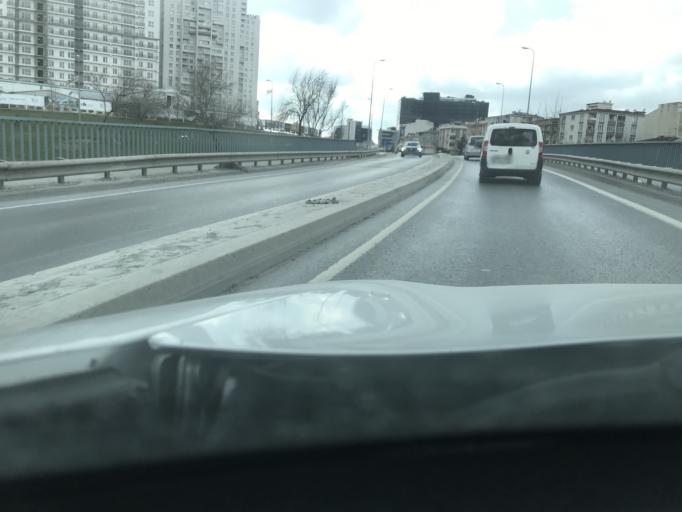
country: TR
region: Istanbul
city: Esenyurt
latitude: 41.0317
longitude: 28.6870
